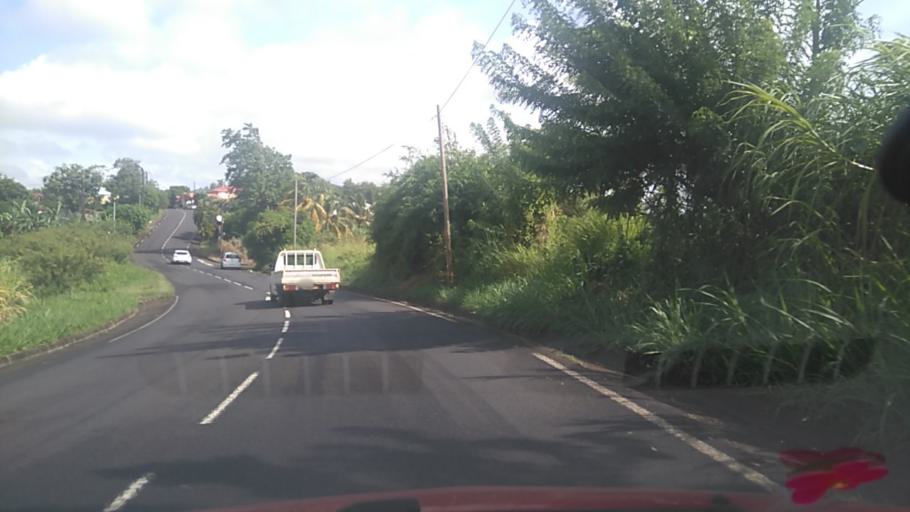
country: MQ
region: Martinique
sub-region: Martinique
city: Le Francois
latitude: 14.5927
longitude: -60.9201
